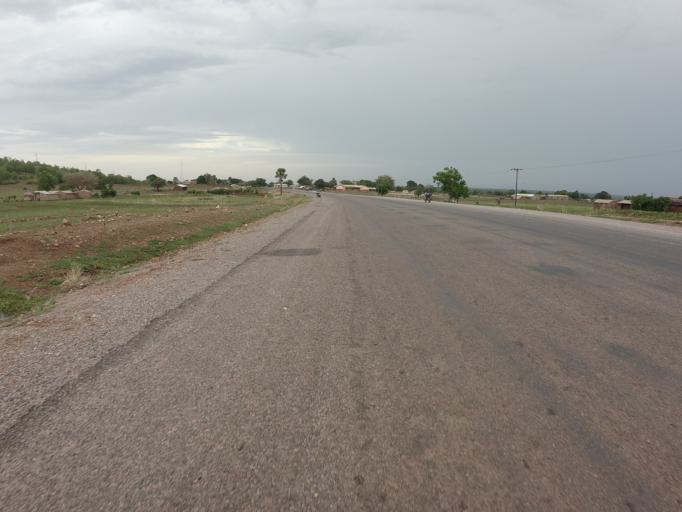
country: GH
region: Upper East
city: Bolgatanga
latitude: 10.8433
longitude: -0.6884
